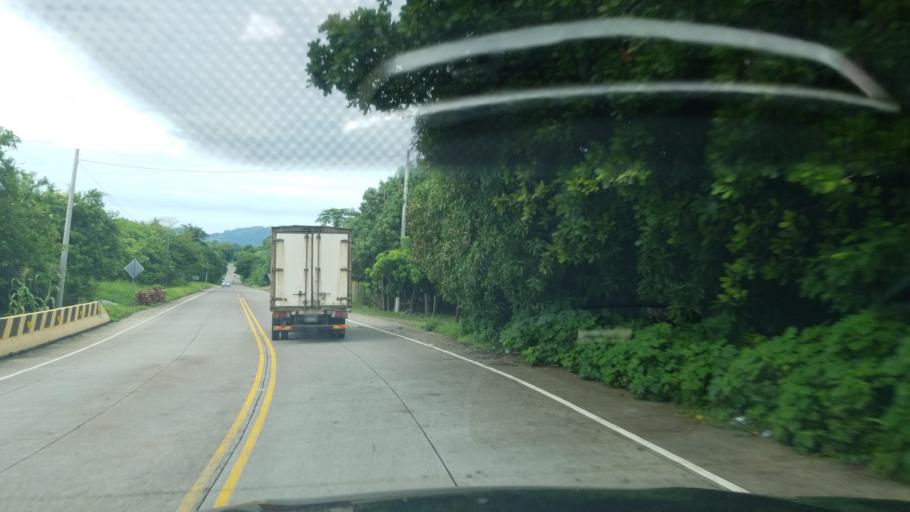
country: HN
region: Choluteca
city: Pespire
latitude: 13.6496
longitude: -87.3681
